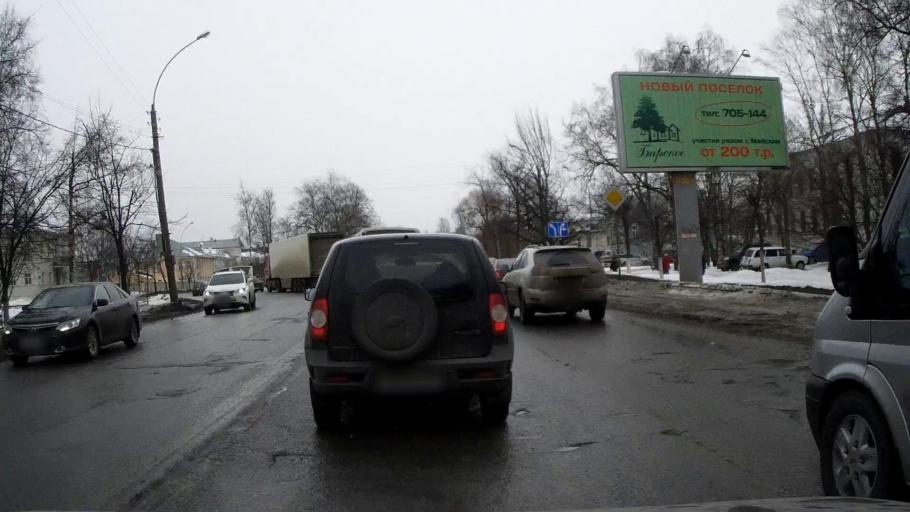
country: RU
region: Vologda
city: Vologda
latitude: 59.2224
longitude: 39.8826
